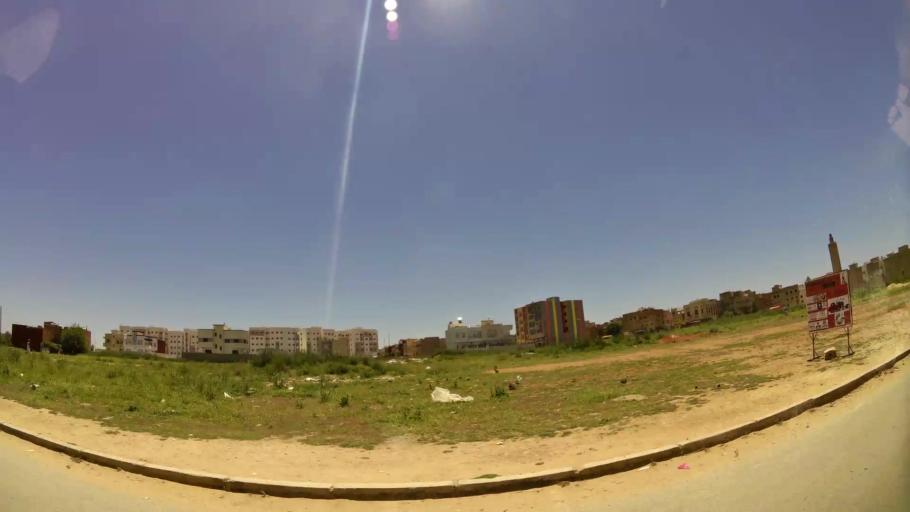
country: MA
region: Meknes-Tafilalet
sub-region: Meknes
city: Meknes
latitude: 33.8542
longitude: -5.5557
